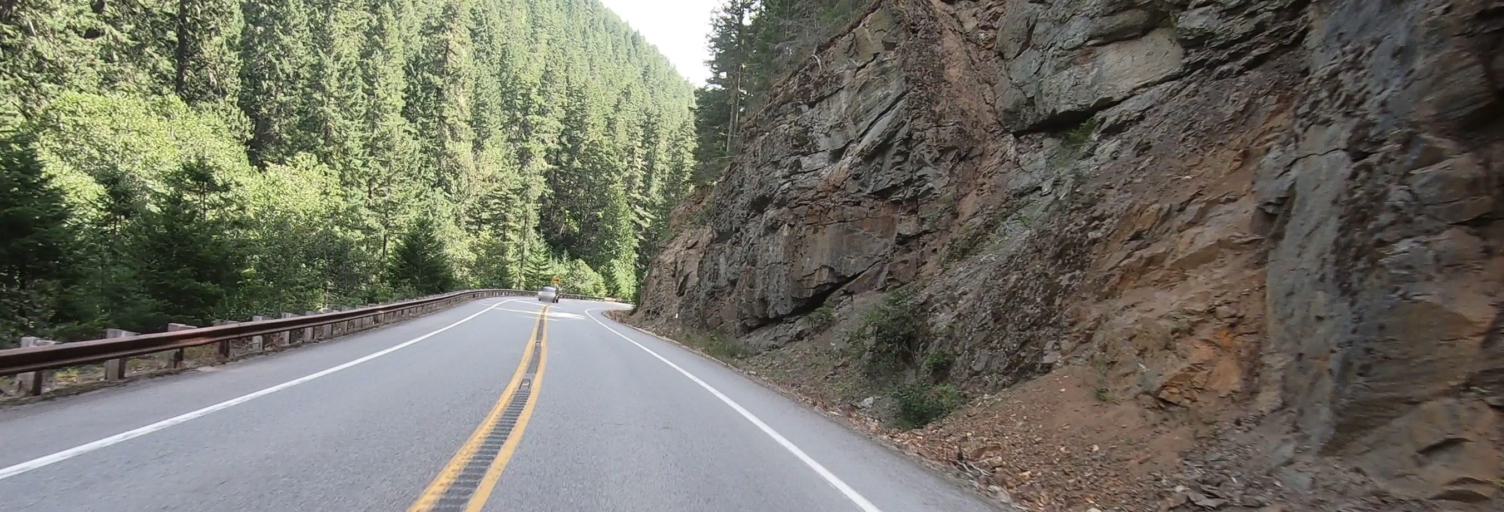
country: US
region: Washington
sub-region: Snohomish County
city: Darrington
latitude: 48.6891
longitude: -120.9122
